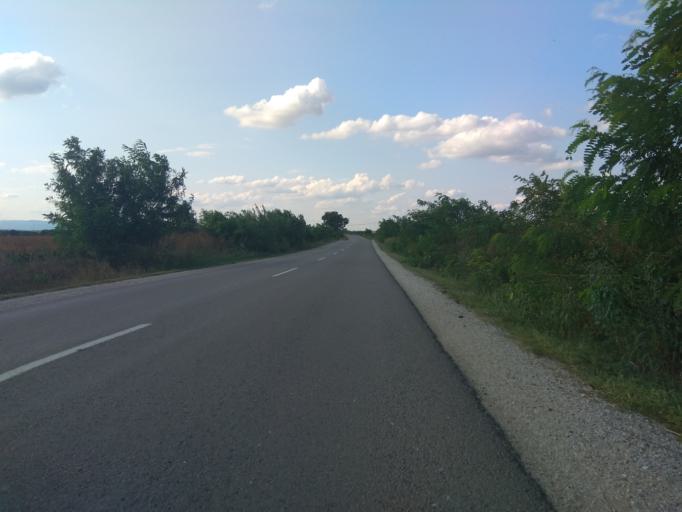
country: HU
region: Borsod-Abauj-Zemplen
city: Hejobaba
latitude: 47.9005
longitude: 20.8905
